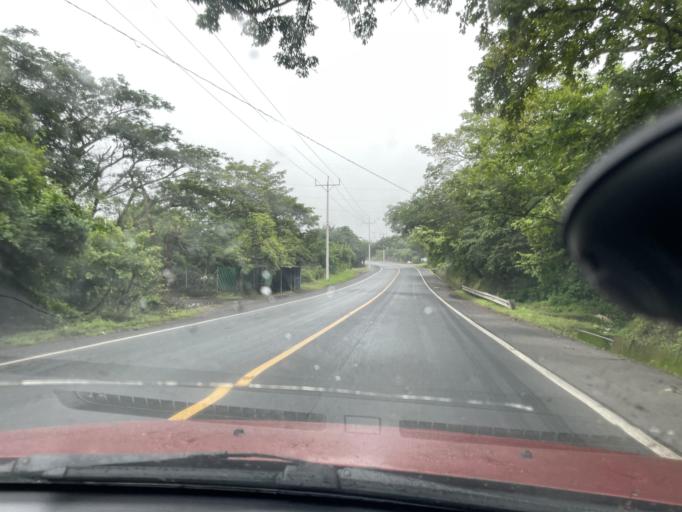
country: SV
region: San Miguel
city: San Miguel
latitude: 13.5356
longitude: -88.1351
